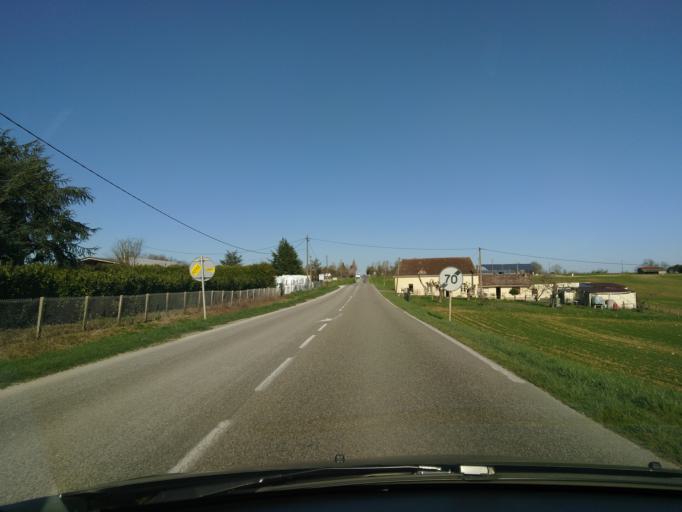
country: FR
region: Aquitaine
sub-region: Departement du Lot-et-Garonne
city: Cancon
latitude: 44.5484
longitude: 0.6259
